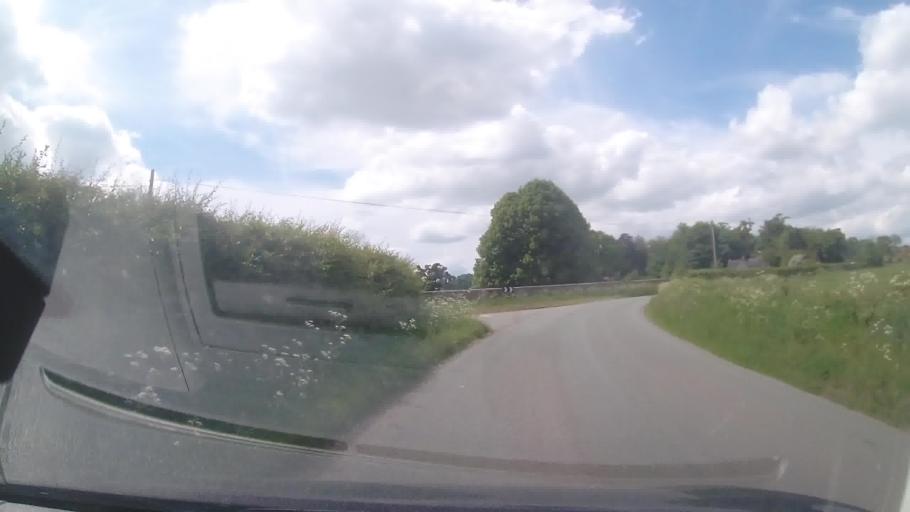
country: GB
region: England
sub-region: Shropshire
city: Clive
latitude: 52.8062
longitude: -2.6842
